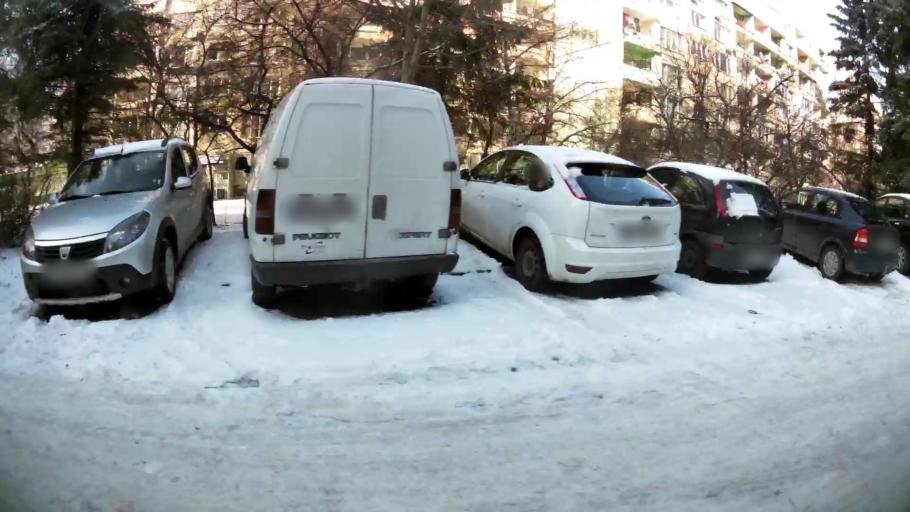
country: BG
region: Sofia-Capital
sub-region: Stolichna Obshtina
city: Sofia
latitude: 42.6604
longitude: 23.3436
